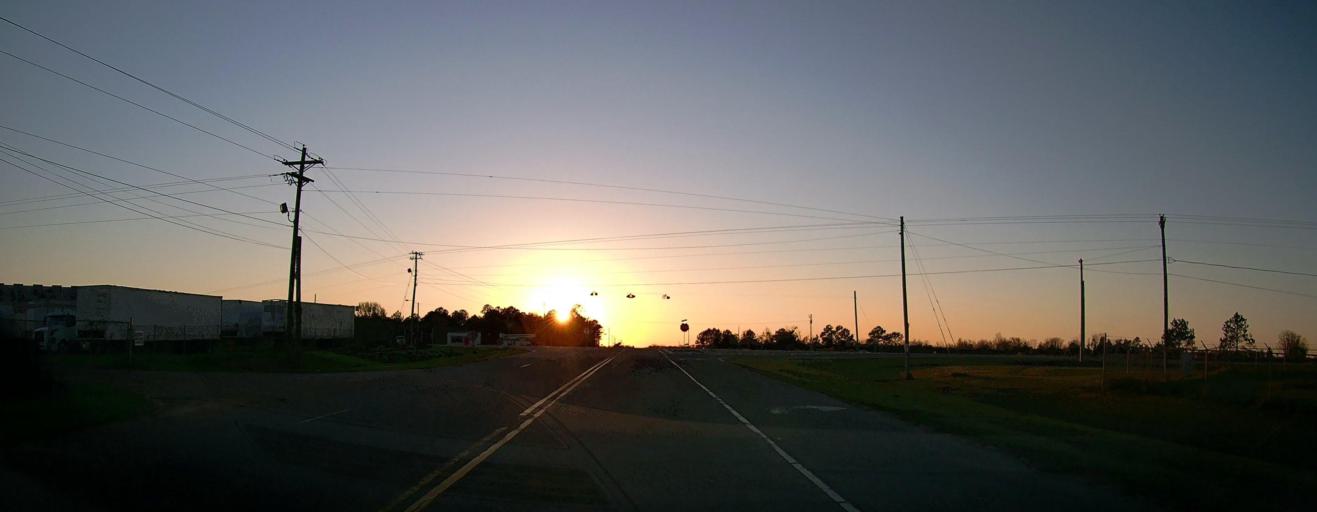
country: US
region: Georgia
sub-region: Crisp County
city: Cordele
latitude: 31.9554
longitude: -83.8070
